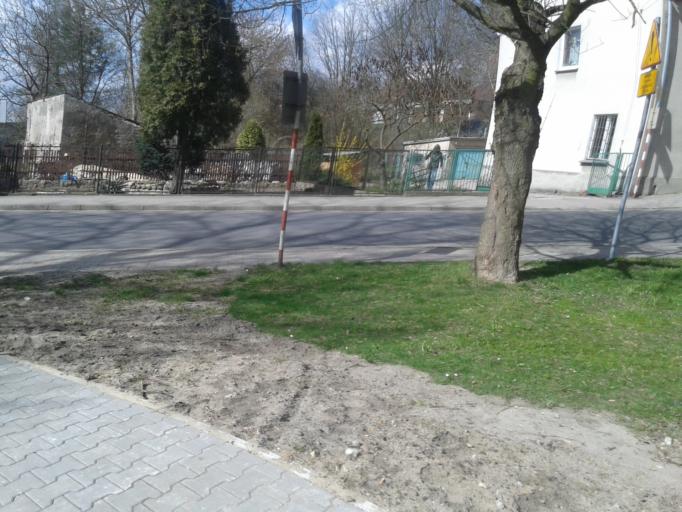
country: PL
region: Lower Silesian Voivodeship
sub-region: Powiat olesnicki
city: Miedzyborz
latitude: 51.3967
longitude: 17.6644
